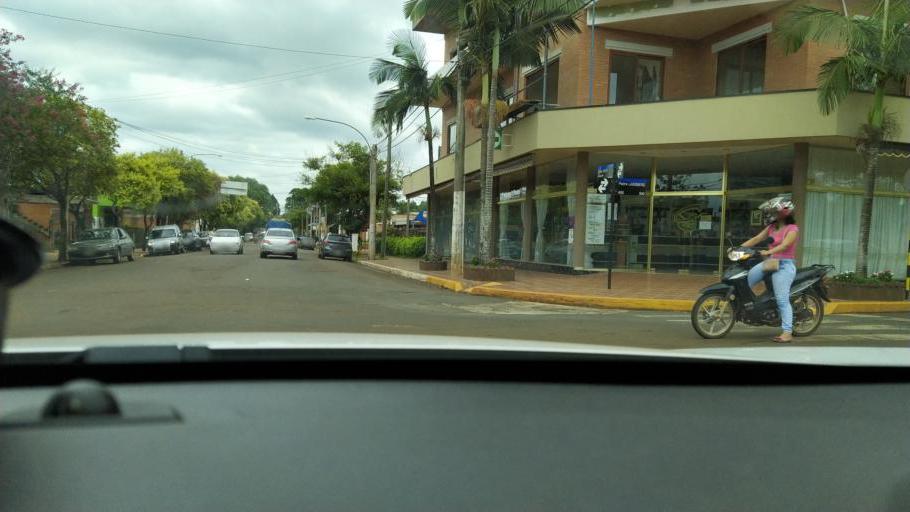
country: AR
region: Misiones
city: Puerto Rico
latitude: -26.8166
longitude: -55.0223
